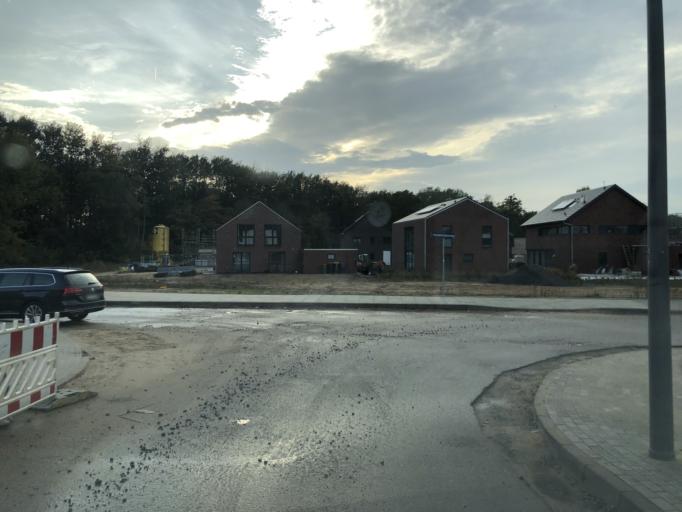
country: DE
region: Lower Saxony
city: Neu Wulmstorf
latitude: 53.4636
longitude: 9.8138
